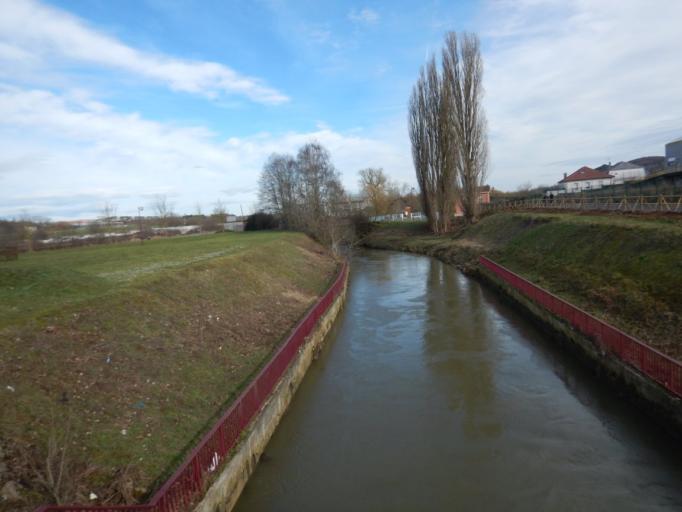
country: FR
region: Lorraine
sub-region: Departement de Meurthe-et-Moselle
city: Longlaville
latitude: 49.5334
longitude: 5.7919
